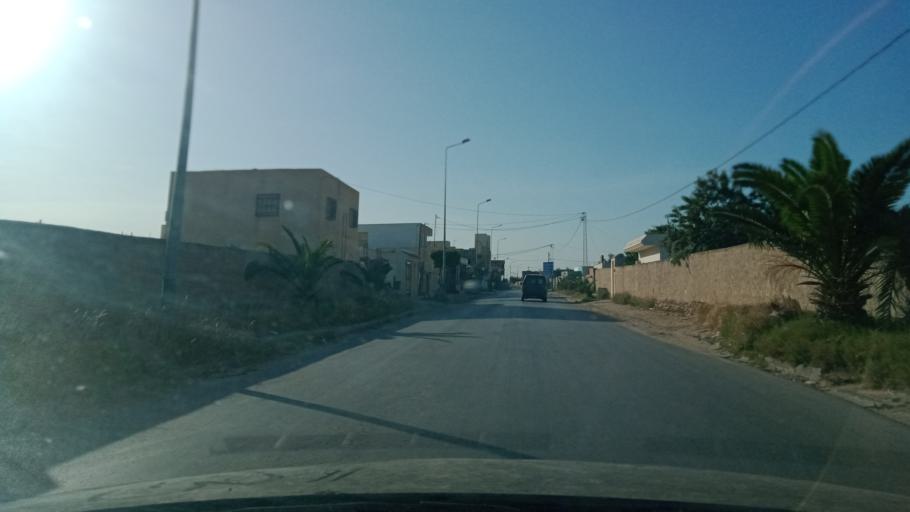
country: TN
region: Safaqis
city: Al Qarmadah
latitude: 34.8198
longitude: 10.7422
